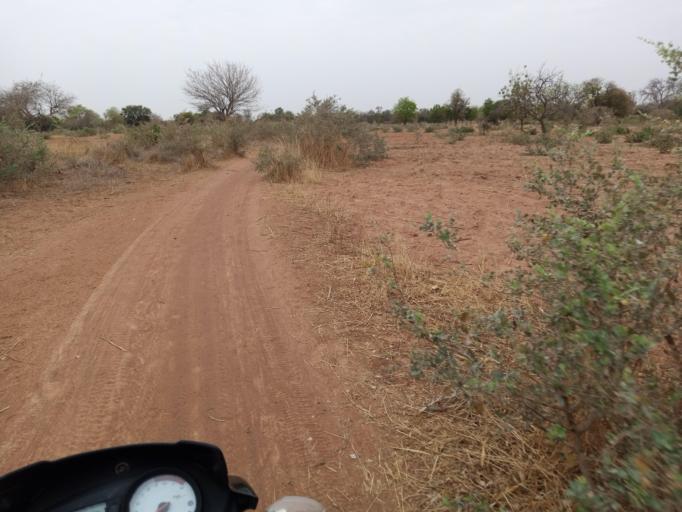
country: BF
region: Boucle du Mouhoun
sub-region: Province de la Kossi
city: Nouna
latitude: 12.8495
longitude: -4.0772
